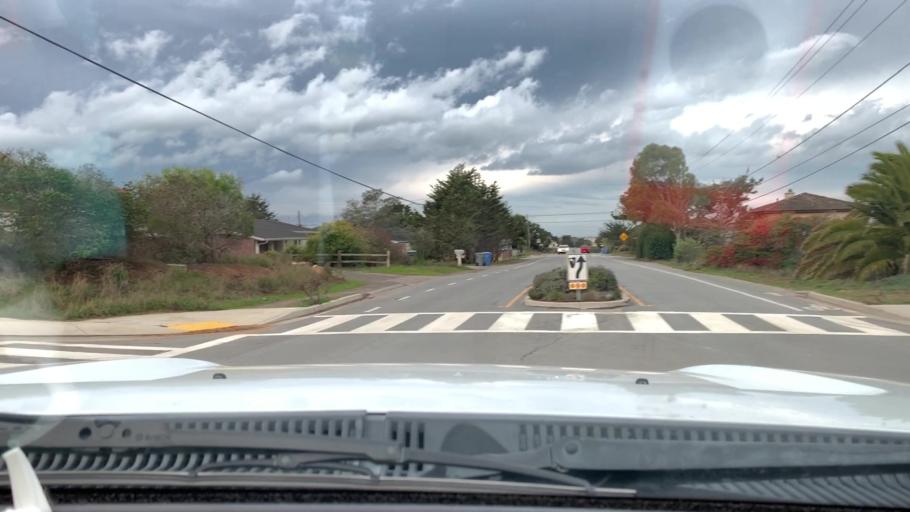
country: US
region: California
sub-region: San Luis Obispo County
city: Los Osos
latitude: 35.3300
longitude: -120.8288
